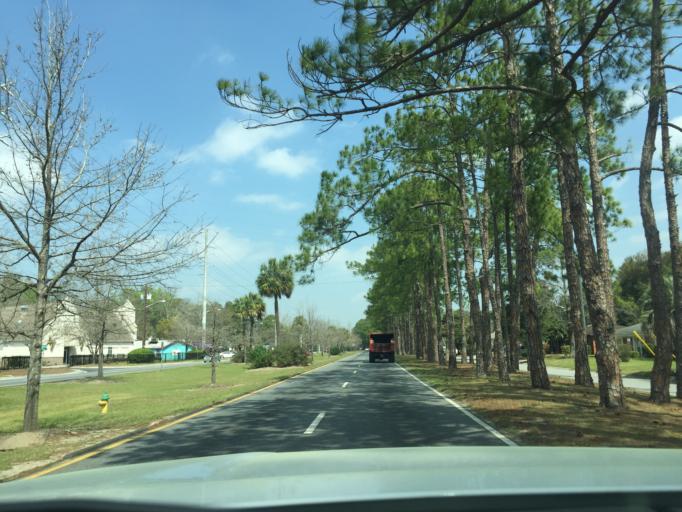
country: US
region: Georgia
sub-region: Chatham County
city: Savannah
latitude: 32.0343
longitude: -81.1132
